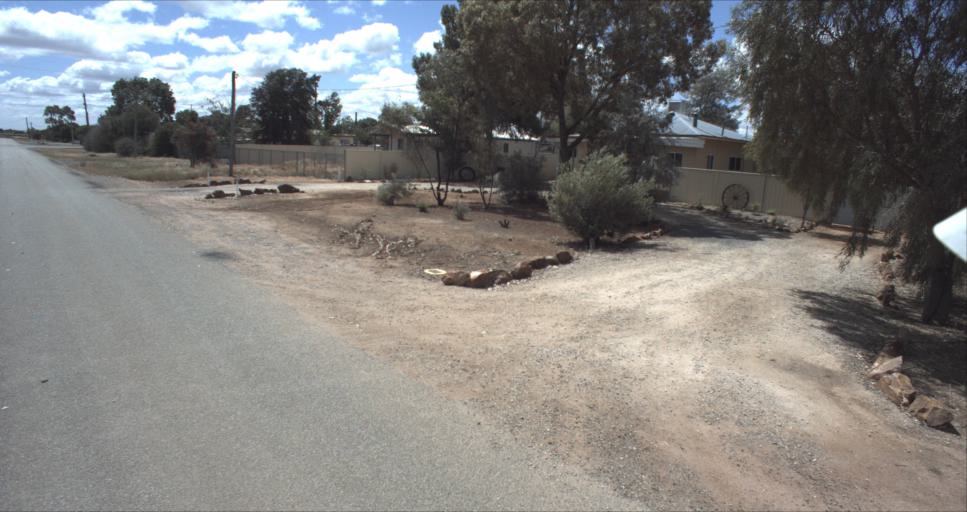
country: AU
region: New South Wales
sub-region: Murrumbidgee Shire
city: Darlington Point
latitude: -34.5133
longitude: 146.1844
